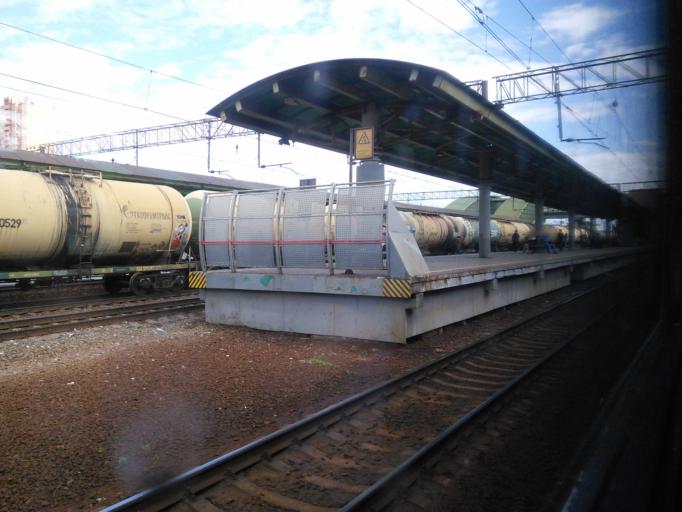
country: RU
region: Moskovskaya
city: Lyubertsy
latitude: 55.6829
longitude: 37.8958
